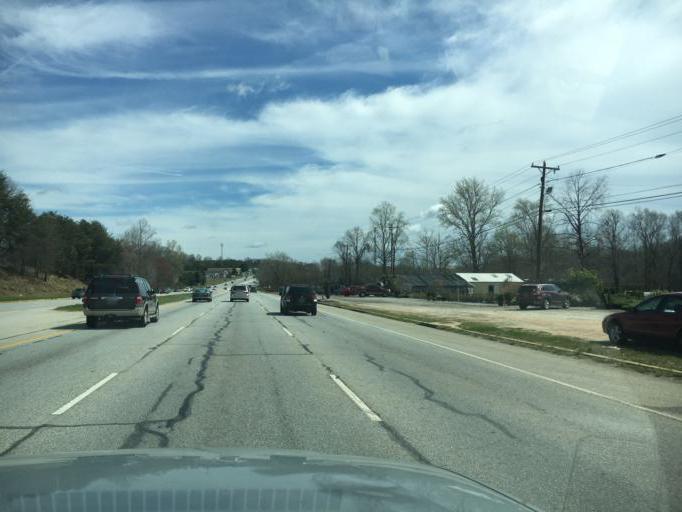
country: US
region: South Carolina
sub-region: Greenville County
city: Taylors
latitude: 34.9243
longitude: -82.3051
